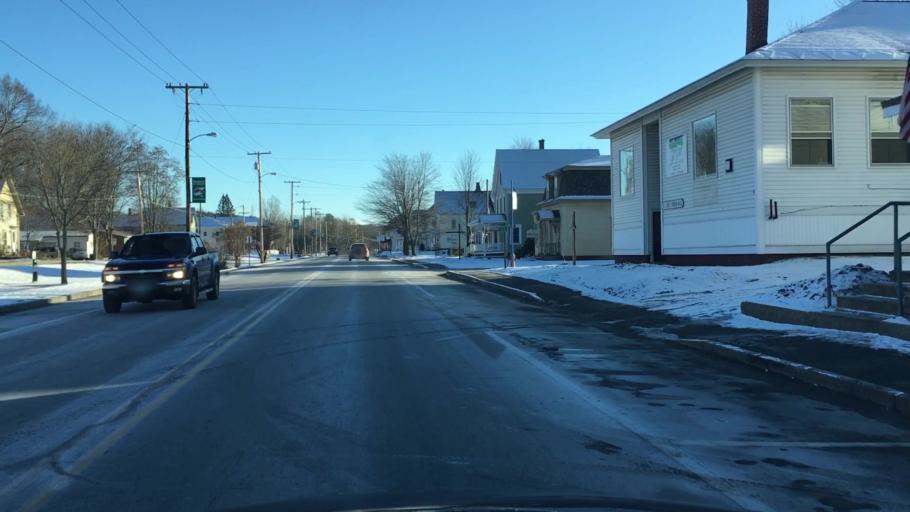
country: US
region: New Hampshire
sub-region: Grafton County
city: Woodsville
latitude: 44.1507
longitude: -72.0357
